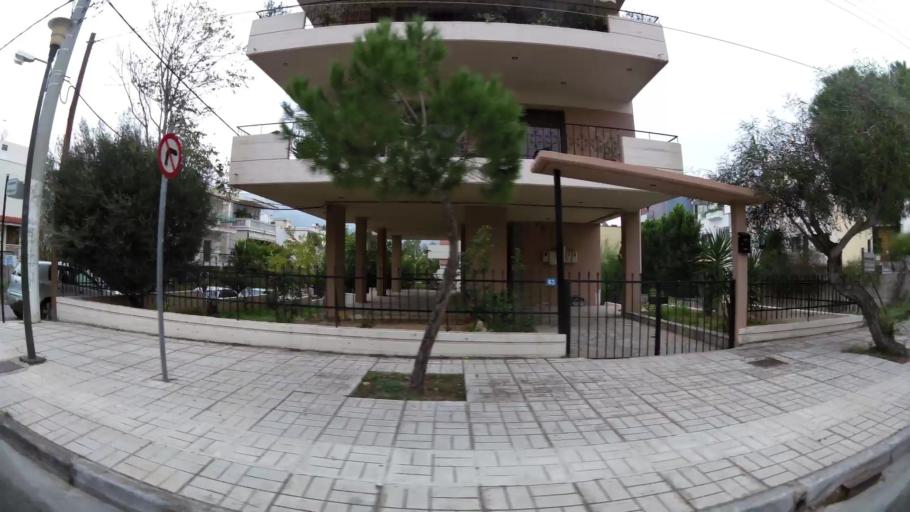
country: GR
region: Attica
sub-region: Nomarchia Athinas
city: Alimos
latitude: 37.9111
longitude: 23.7346
